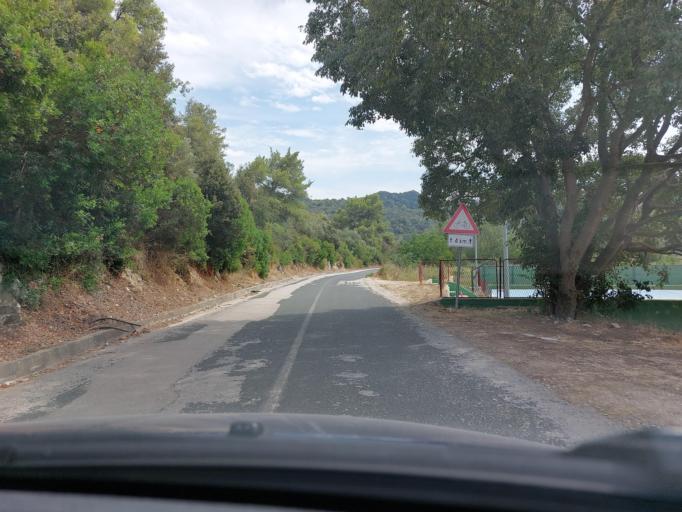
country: HR
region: Dubrovacko-Neretvanska
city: Smokvica
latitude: 42.7649
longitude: 16.8955
